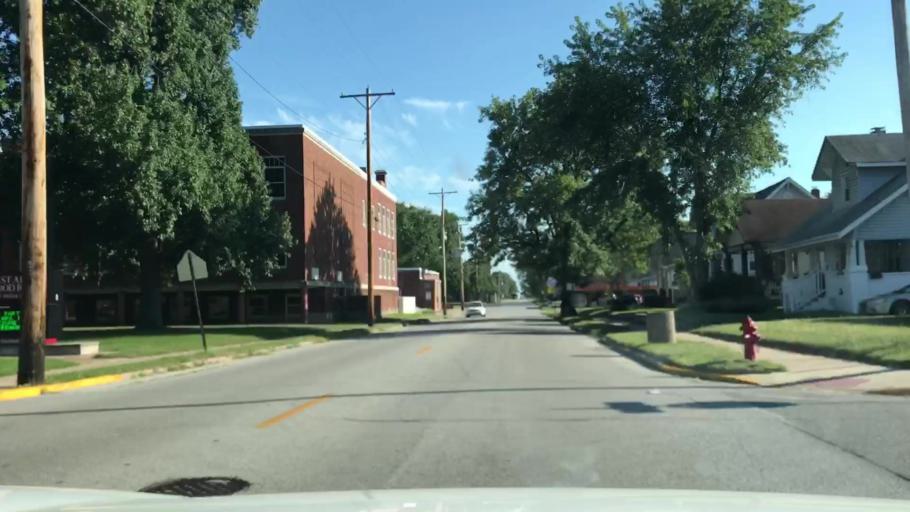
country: US
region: Illinois
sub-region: Madison County
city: Wood River
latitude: 38.8724
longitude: -90.0988
